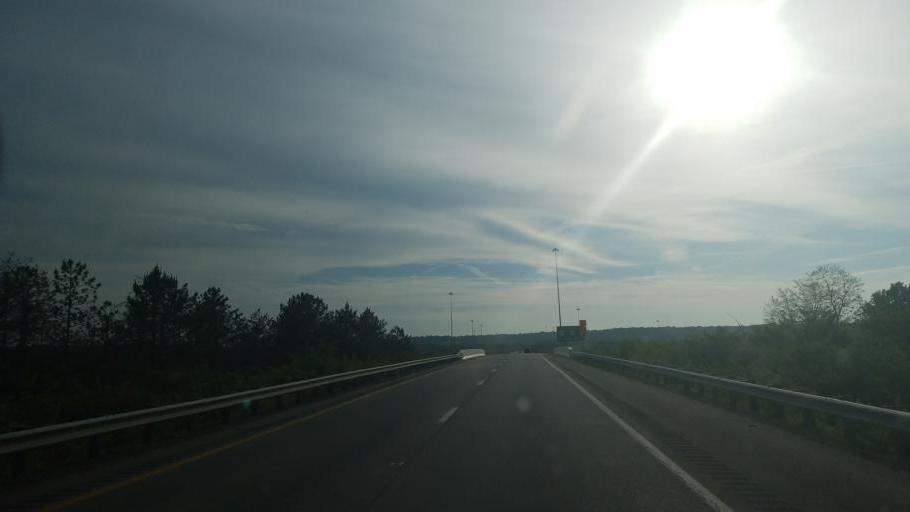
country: US
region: Ohio
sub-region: Ross County
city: Chillicothe
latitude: 39.3495
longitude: -82.9679
